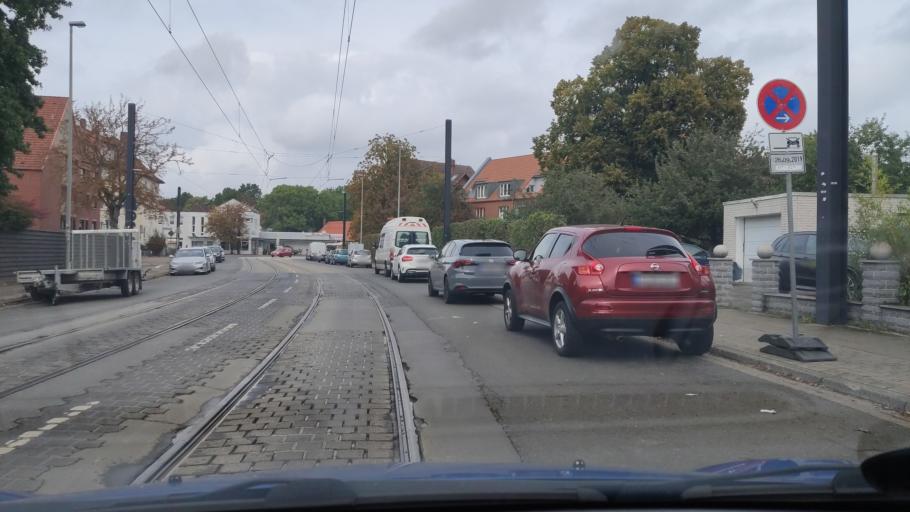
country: DE
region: Lower Saxony
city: Ronnenberg
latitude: 52.3539
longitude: 9.6700
